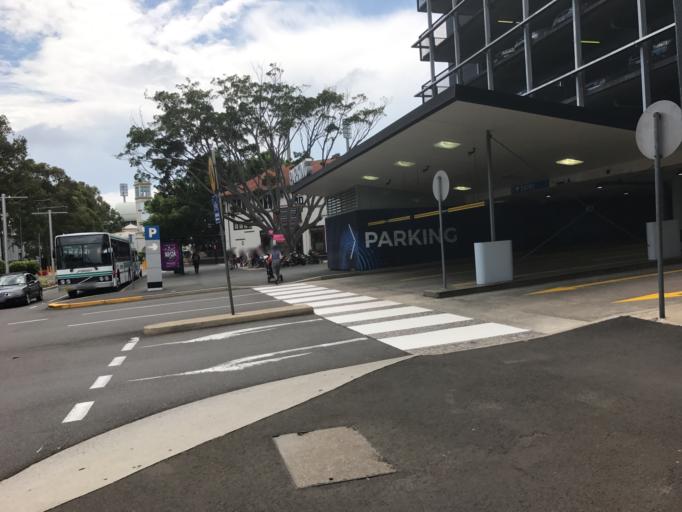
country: AU
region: New South Wales
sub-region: Woollahra
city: Paddington
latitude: -33.8951
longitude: 151.2251
